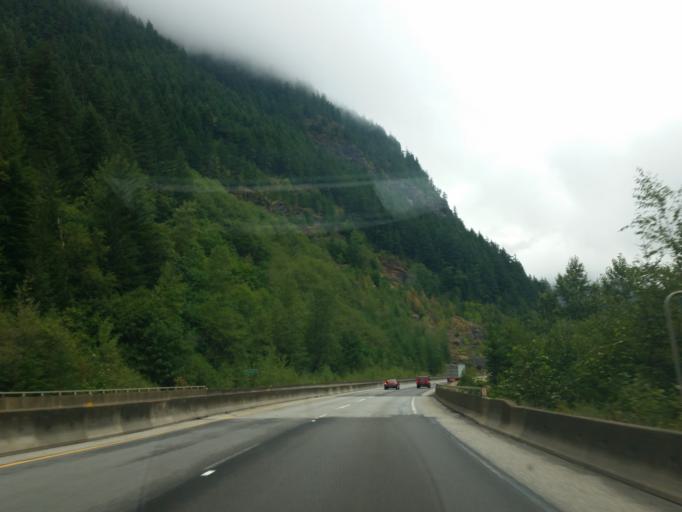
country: CA
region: British Columbia
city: Hope
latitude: 49.4387
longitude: -121.3023
